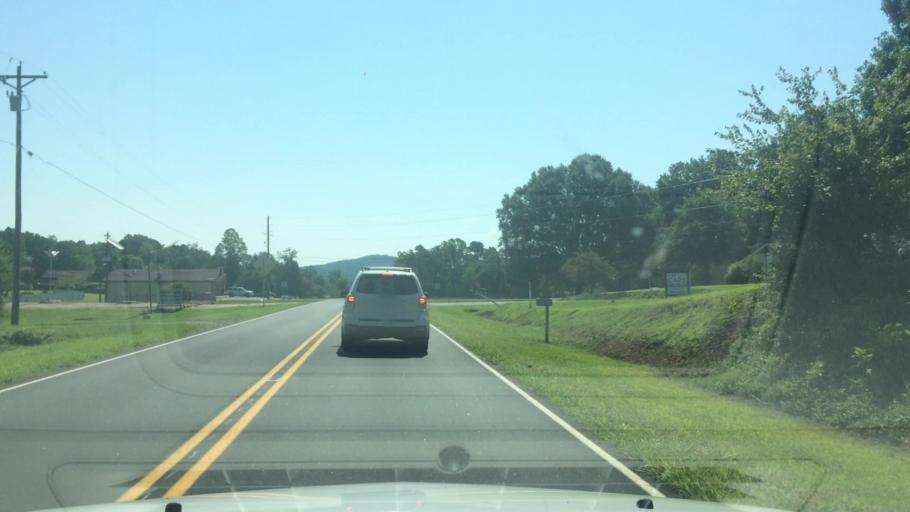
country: US
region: North Carolina
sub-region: Caldwell County
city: Sawmills
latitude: 35.9075
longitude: -81.4033
